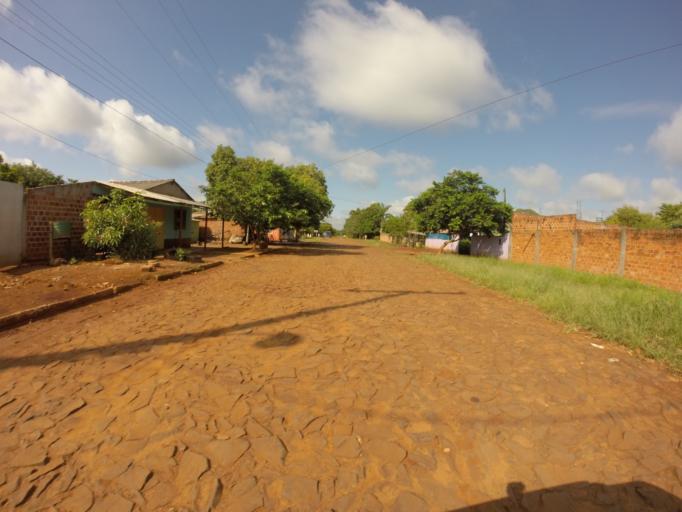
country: PY
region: Alto Parana
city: Ciudad del Este
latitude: -25.3951
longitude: -54.6450
